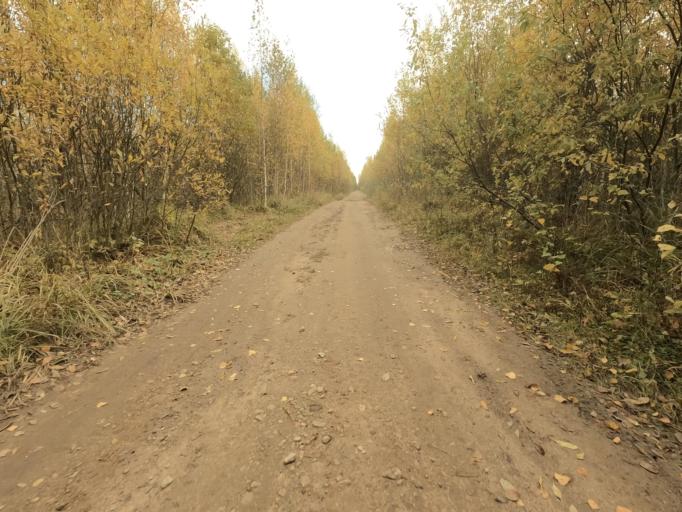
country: RU
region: Novgorod
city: Pankovka
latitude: 58.8774
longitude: 30.8641
